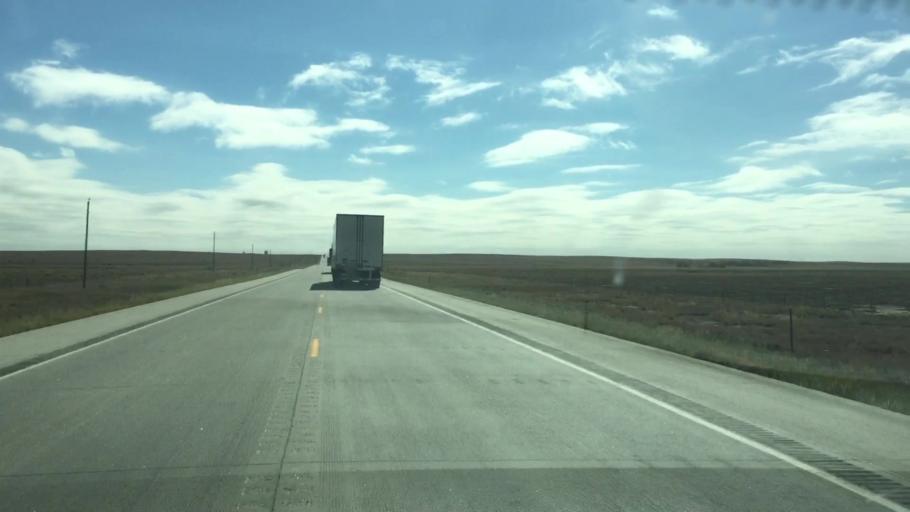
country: US
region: Colorado
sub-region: Lincoln County
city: Hugo
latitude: 39.0466
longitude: -103.3444
